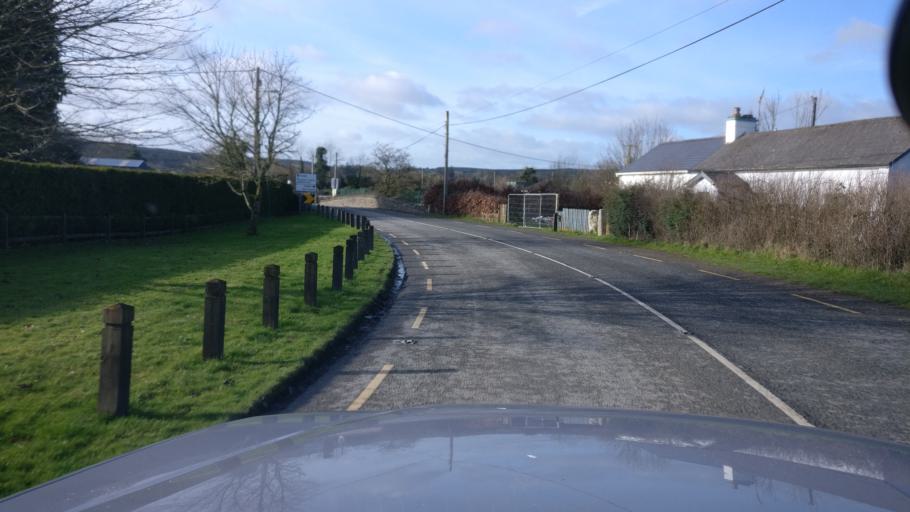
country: IE
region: Leinster
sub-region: Kilkenny
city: Castlecomer
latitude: 52.8898
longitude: -7.1619
